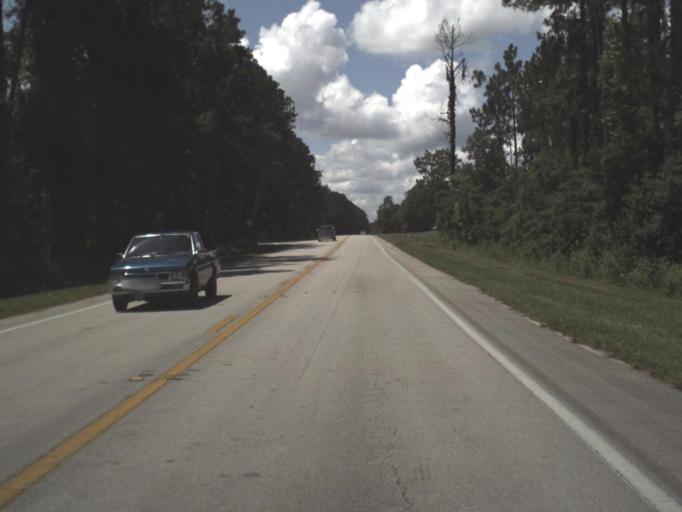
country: US
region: Florida
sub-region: Putnam County
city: Crescent City
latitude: 29.3914
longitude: -81.5088
